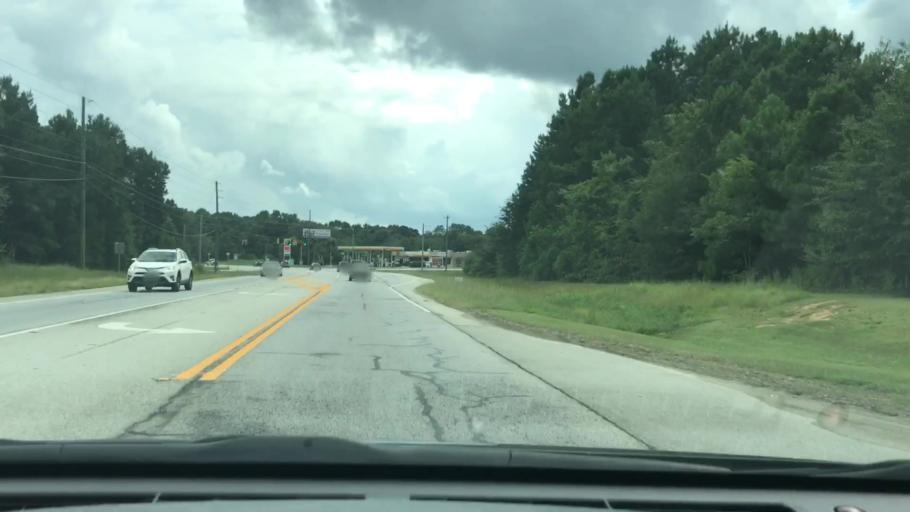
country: US
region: Georgia
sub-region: Walton County
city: Loganville
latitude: 33.8076
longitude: -83.8743
